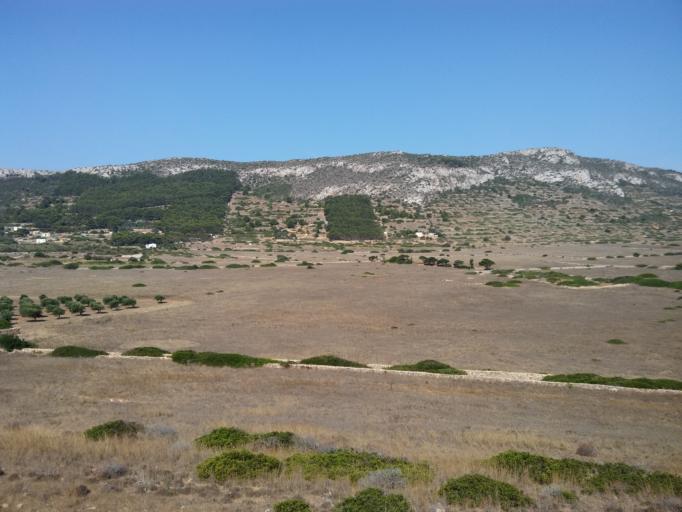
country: IT
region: Sicily
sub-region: Trapani
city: Favignana
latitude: 37.9935
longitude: 12.3460
